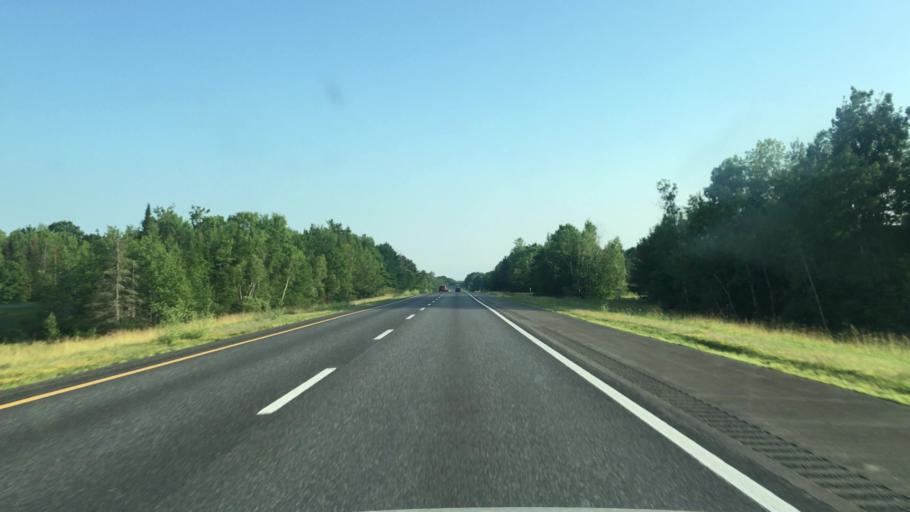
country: US
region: Maine
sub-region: Sagadahoc County
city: Richmond
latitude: 44.1450
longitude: -69.8416
